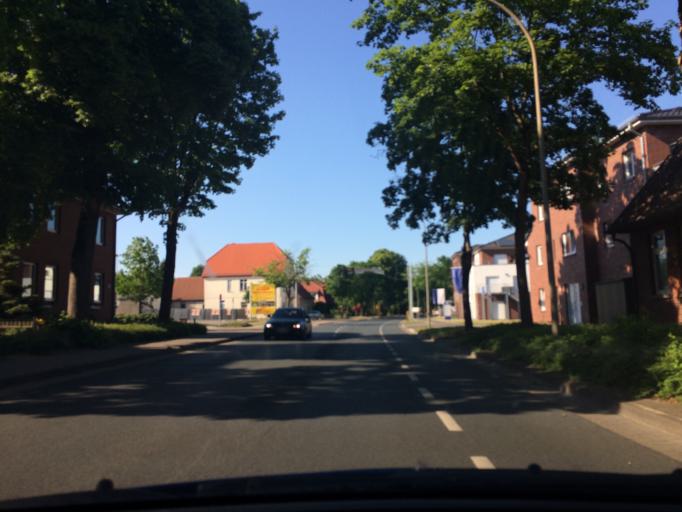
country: DE
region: Lower Saxony
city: Soltau
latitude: 52.9937
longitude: 9.8357
